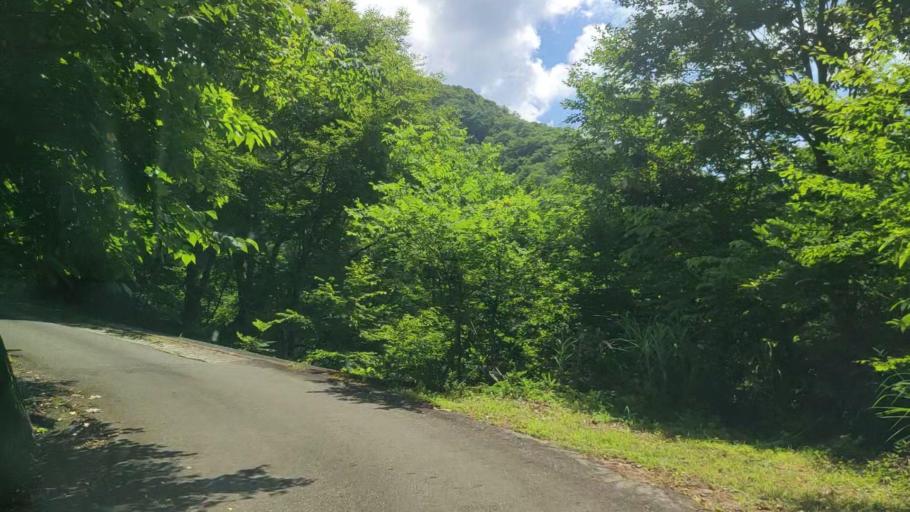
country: JP
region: Fukui
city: Ono
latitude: 35.7903
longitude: 136.5039
